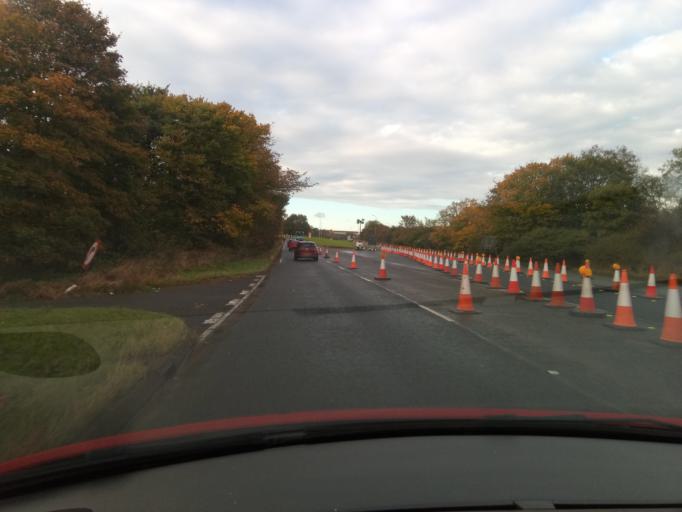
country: GB
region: England
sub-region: Darlington
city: Heighington
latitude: 54.5747
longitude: -1.6114
